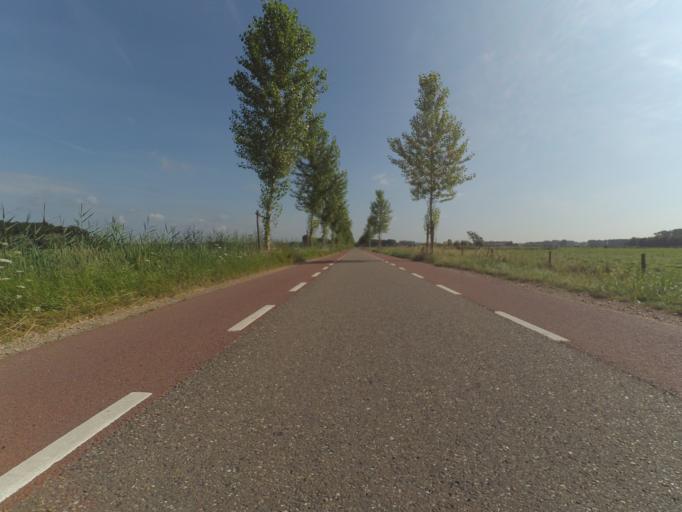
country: NL
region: Utrecht
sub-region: Gemeente Wijk bij Duurstede
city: Wijk bij Duurstede
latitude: 52.0022
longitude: 5.3624
